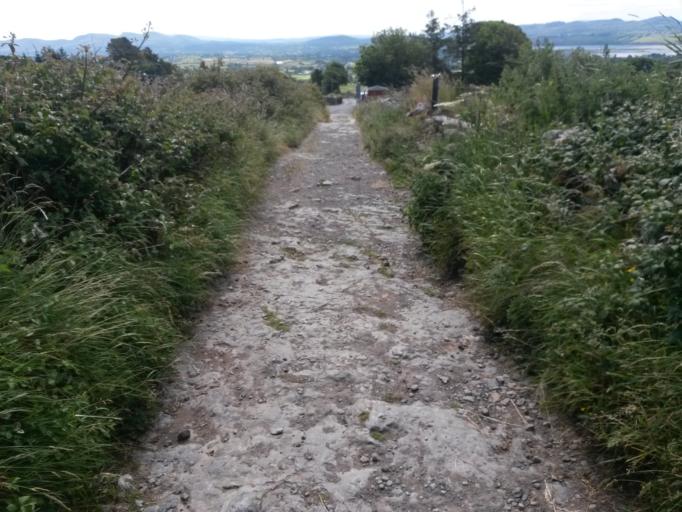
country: IE
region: Connaught
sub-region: Sligo
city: Strandhill
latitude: 54.2536
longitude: -8.5587
